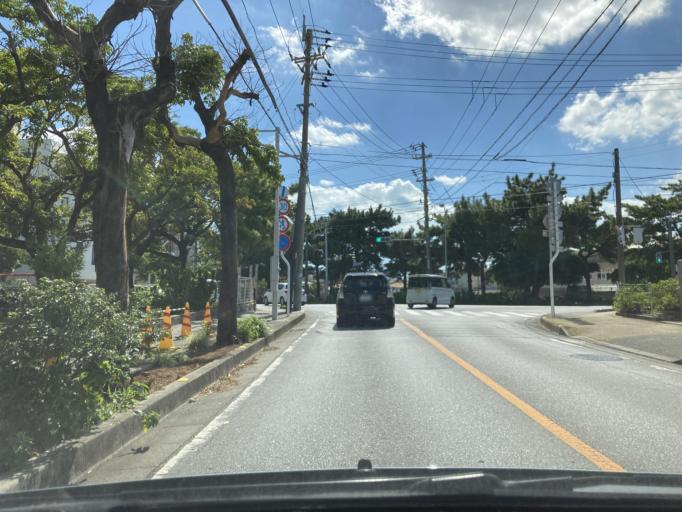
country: JP
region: Okinawa
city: Naha-shi
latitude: 26.2068
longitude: 127.6860
